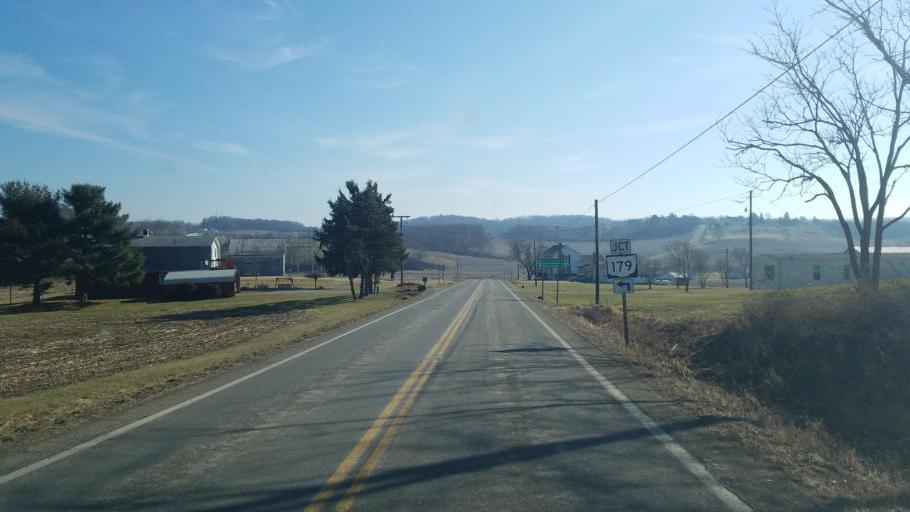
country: US
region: Ohio
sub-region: Ashland County
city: Loudonville
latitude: 40.6026
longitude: -82.1274
